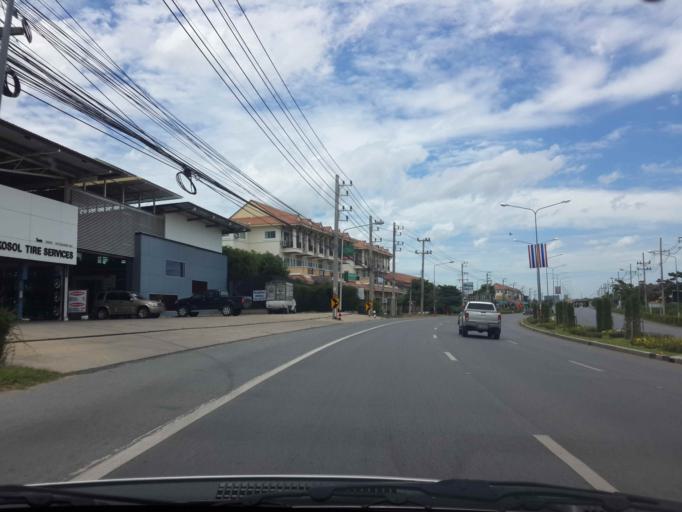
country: TH
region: Prachuap Khiri Khan
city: Hua Hin
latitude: 12.6351
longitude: 99.9485
